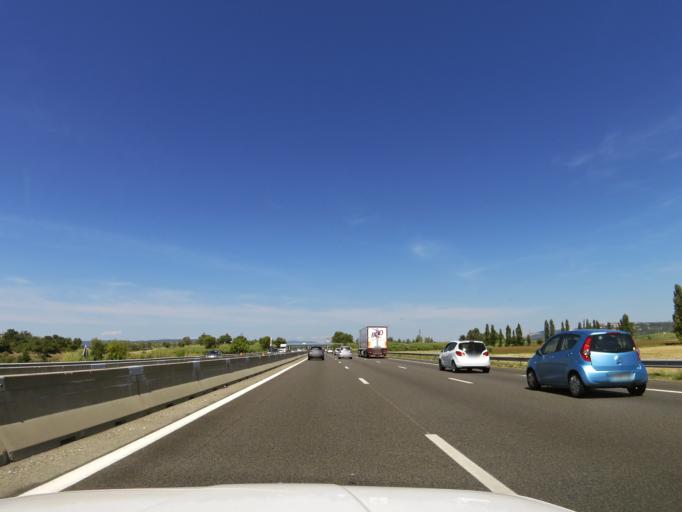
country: FR
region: Rhone-Alpes
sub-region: Departement de la Drome
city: Saint-Paul-Trois-Chateaux
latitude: 44.3613
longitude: 4.7365
